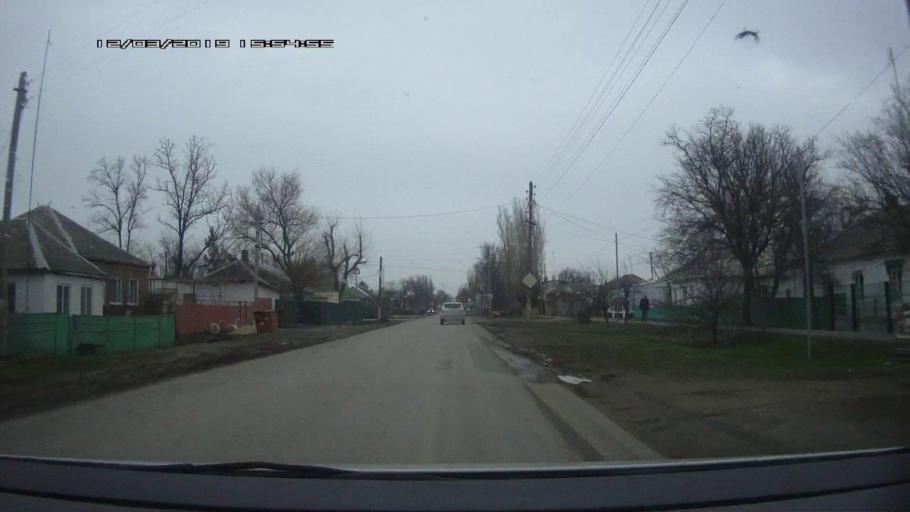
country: RU
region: Rostov
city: Novobataysk
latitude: 46.8936
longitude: 39.7786
